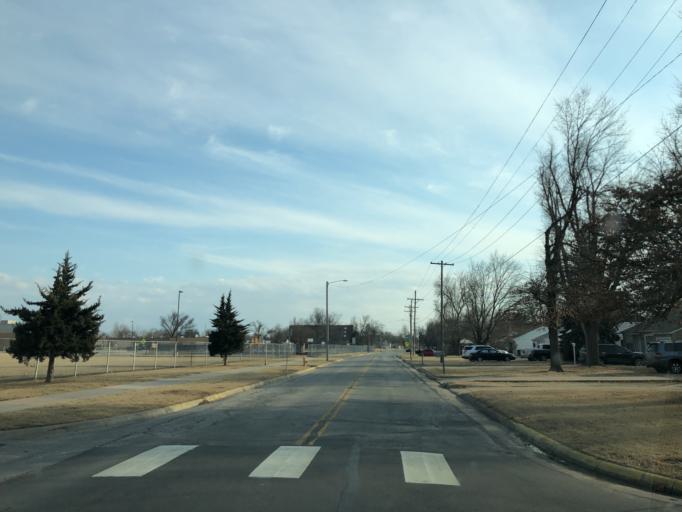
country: US
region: Kansas
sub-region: Reno County
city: Hutchinson
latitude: 38.0856
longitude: -97.9356
